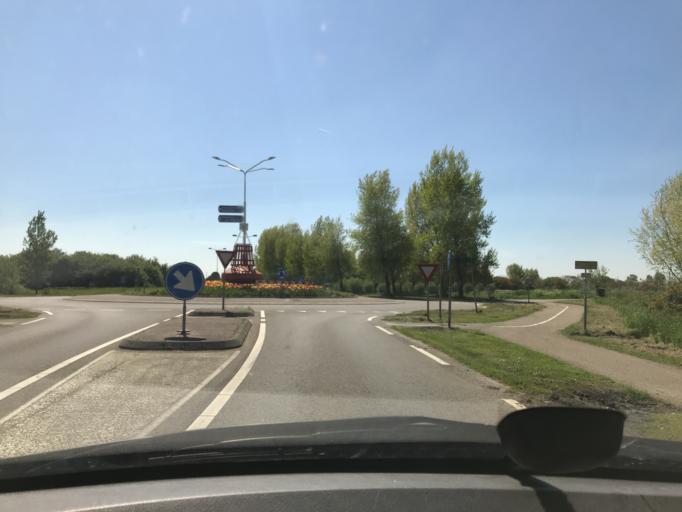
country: NL
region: Zeeland
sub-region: Gemeente Veere
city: Veere
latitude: 51.4988
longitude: 3.6762
